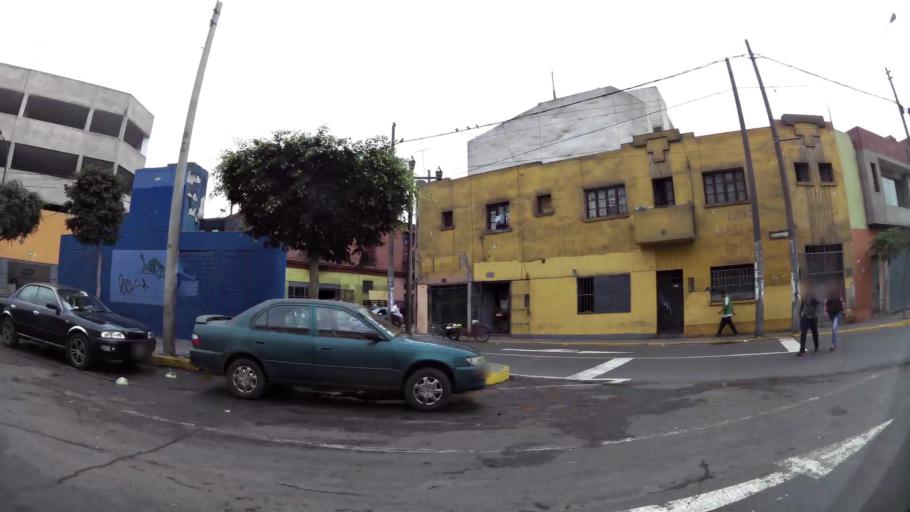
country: PE
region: Lima
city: Lima
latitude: -12.0556
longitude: -77.0333
